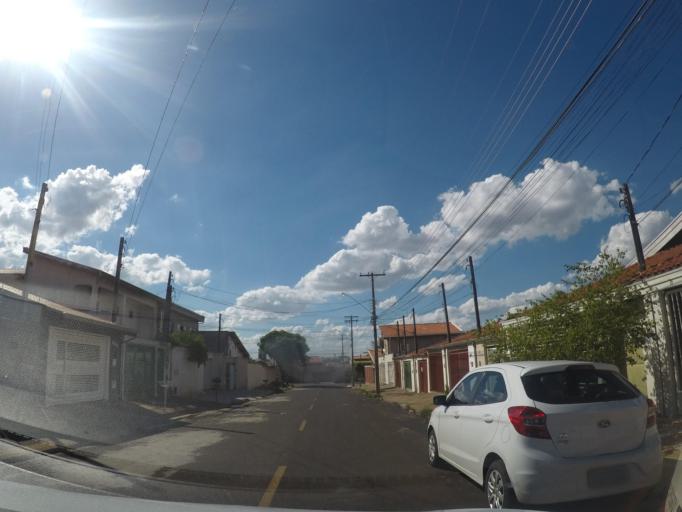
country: BR
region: Sao Paulo
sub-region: Sumare
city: Sumare
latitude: -22.8294
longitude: -47.2787
